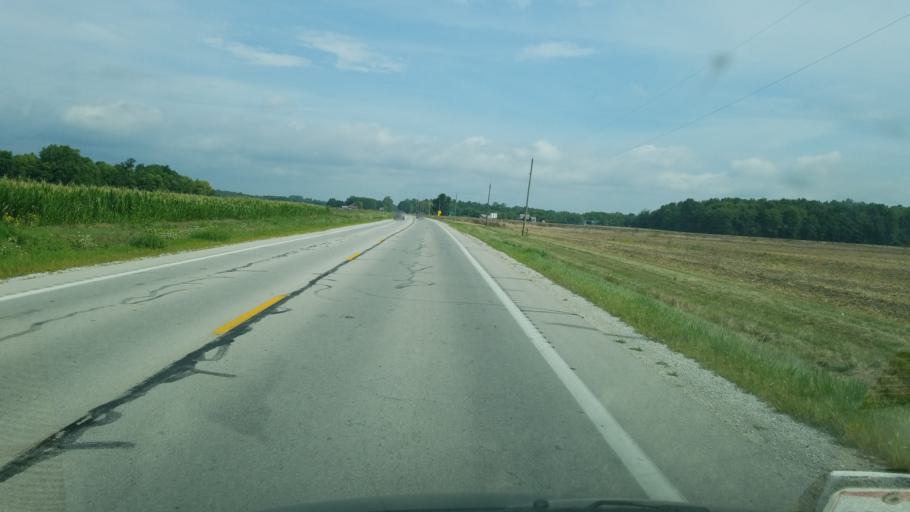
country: US
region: Ohio
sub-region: Sandusky County
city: Ballville
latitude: 41.2541
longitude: -83.1676
